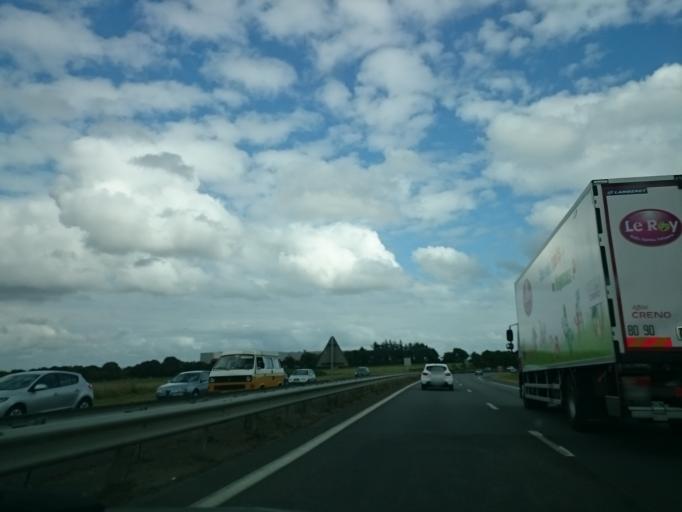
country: FR
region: Brittany
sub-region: Departement du Finistere
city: Gouesnou
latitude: 48.4297
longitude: -4.4389
